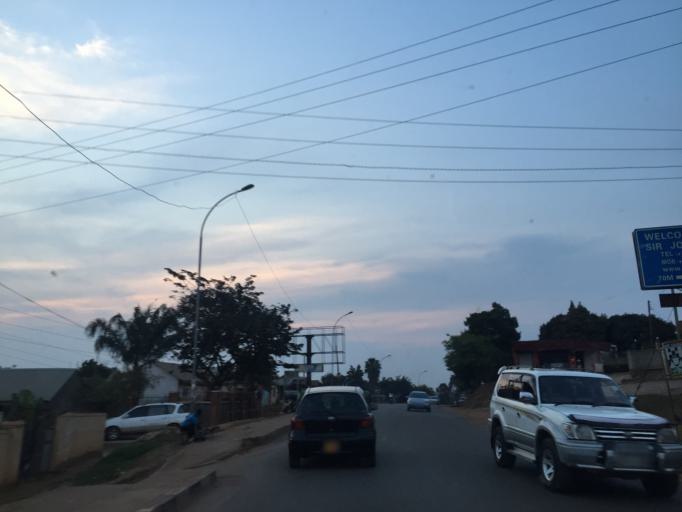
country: UG
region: Central Region
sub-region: Kampala District
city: Kampala
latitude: 0.2590
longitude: 32.6270
